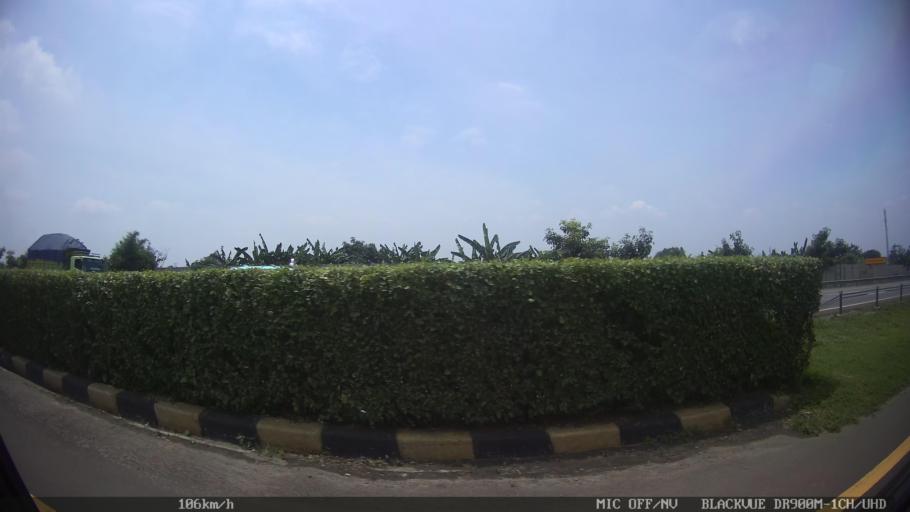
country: ID
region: West Java
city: Kresek
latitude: -6.1767
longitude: 106.3560
